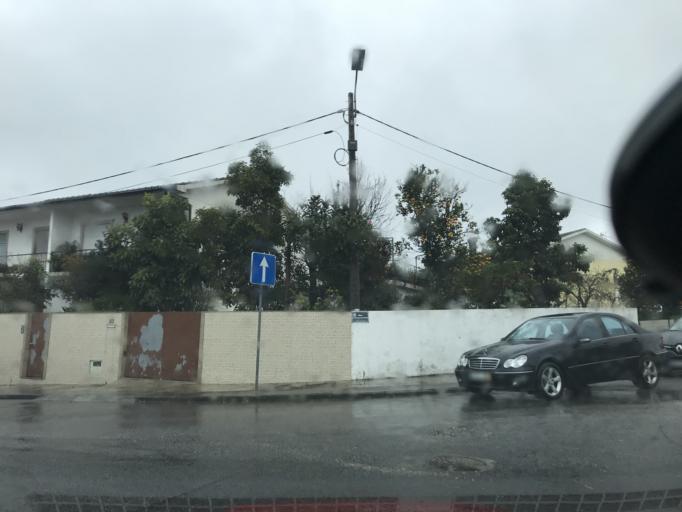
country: PT
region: Braga
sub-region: Vila Nova de Famalicao
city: Vila Nova de Famalicao
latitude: 41.4177
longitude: -8.5127
